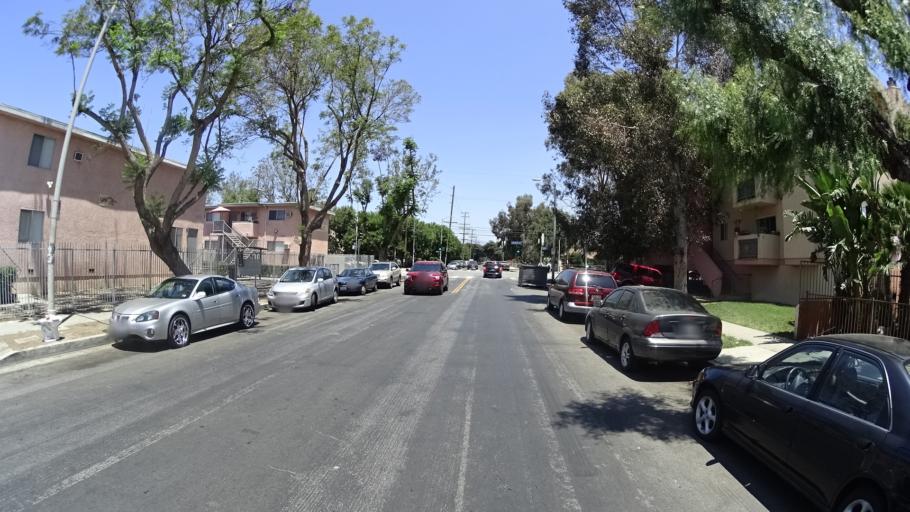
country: US
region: California
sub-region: Los Angeles County
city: Van Nuys
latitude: 34.2349
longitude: -118.4535
